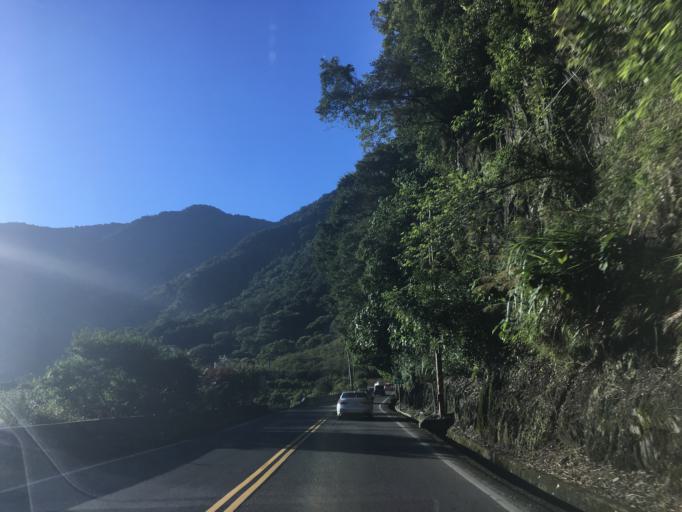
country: TW
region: Taiwan
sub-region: Nantou
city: Puli
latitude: 23.9962
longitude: 121.0699
